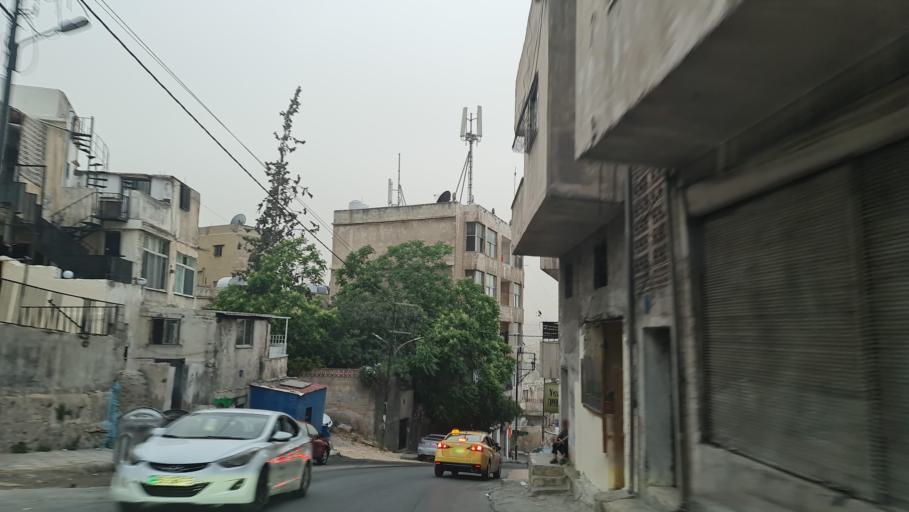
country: JO
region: Amman
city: Amman
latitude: 31.9474
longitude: 35.9420
